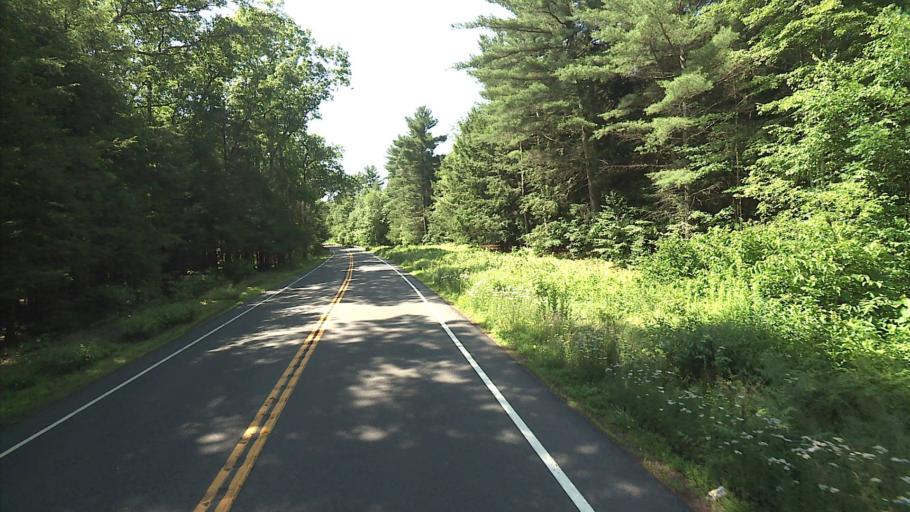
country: US
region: Connecticut
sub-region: Litchfield County
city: Terryville
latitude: 41.7051
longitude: -73.0097
